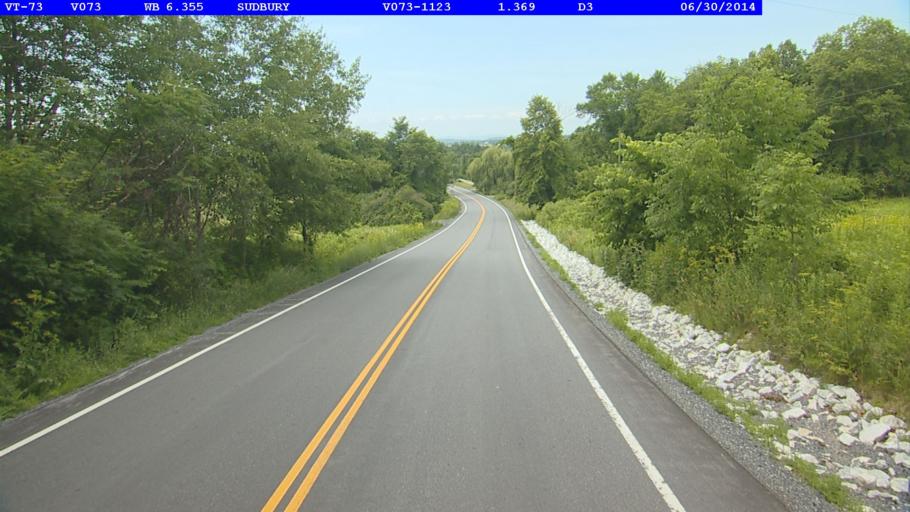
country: US
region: Vermont
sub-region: Rutland County
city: Brandon
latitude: 43.8214
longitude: -73.1742
